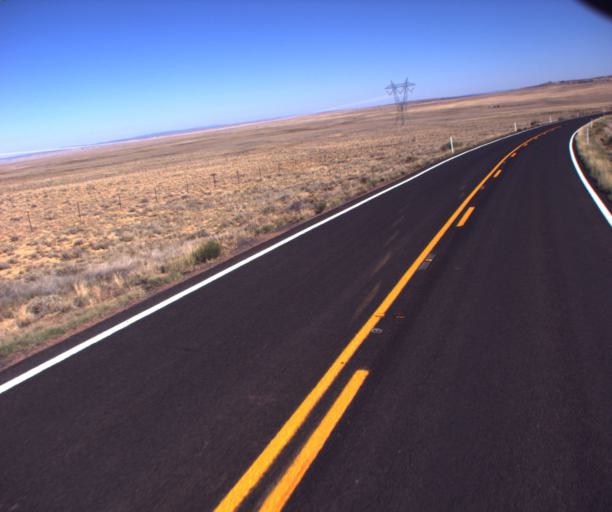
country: US
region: Arizona
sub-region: Coconino County
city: Tuba City
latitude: 35.9696
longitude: -110.8433
